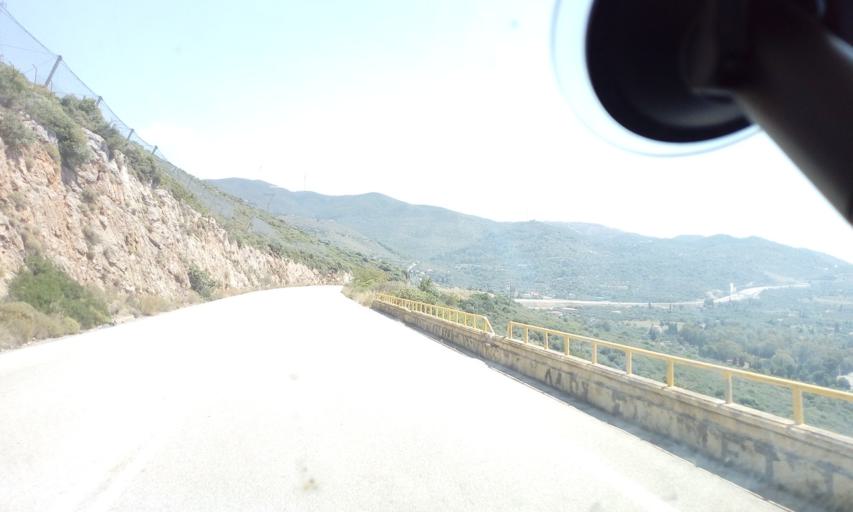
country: GR
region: West Greece
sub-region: Nomos Aitolias kai Akarnanias
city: Antirrio
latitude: 38.3502
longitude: 21.6926
